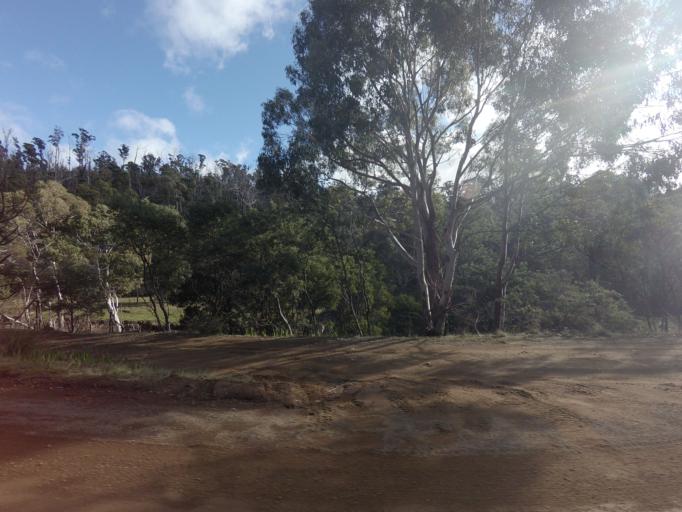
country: AU
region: Tasmania
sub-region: Derwent Valley
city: New Norfolk
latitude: -42.8115
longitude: 147.1309
